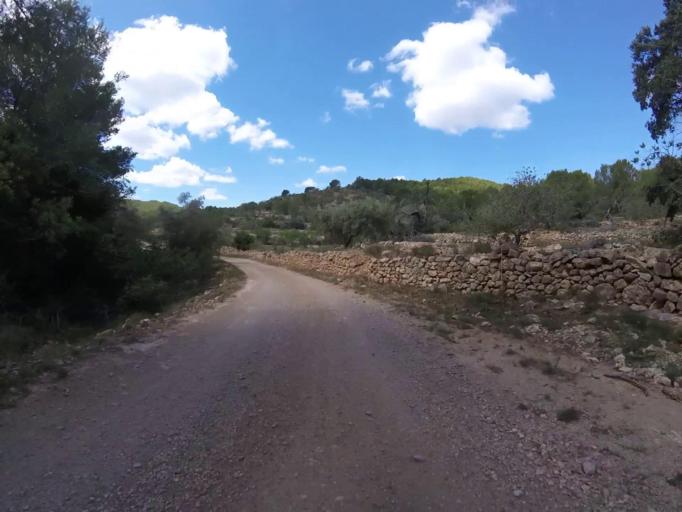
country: ES
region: Valencia
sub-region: Provincia de Castello
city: Santa Magdalena de Pulpis
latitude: 40.3159
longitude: 0.3307
